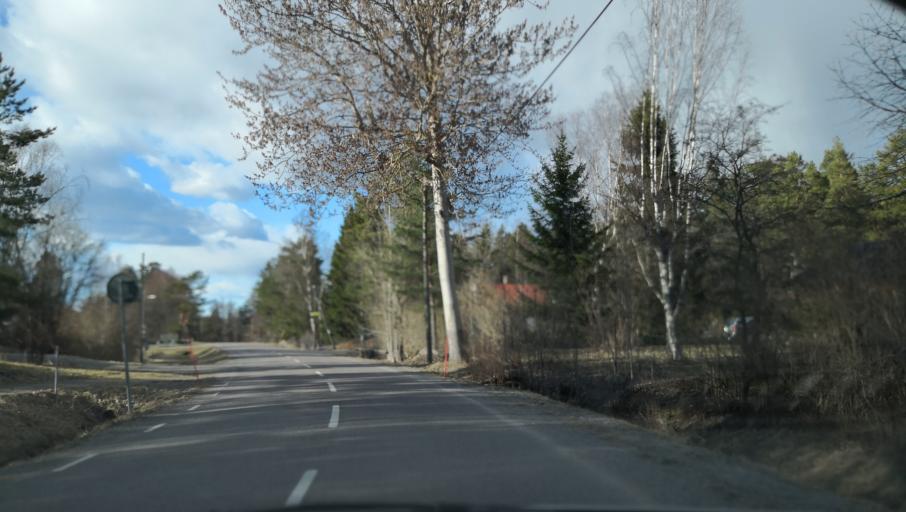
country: SE
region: Stockholm
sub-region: Varmdo Kommun
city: Hemmesta
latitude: 59.2827
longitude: 18.4943
